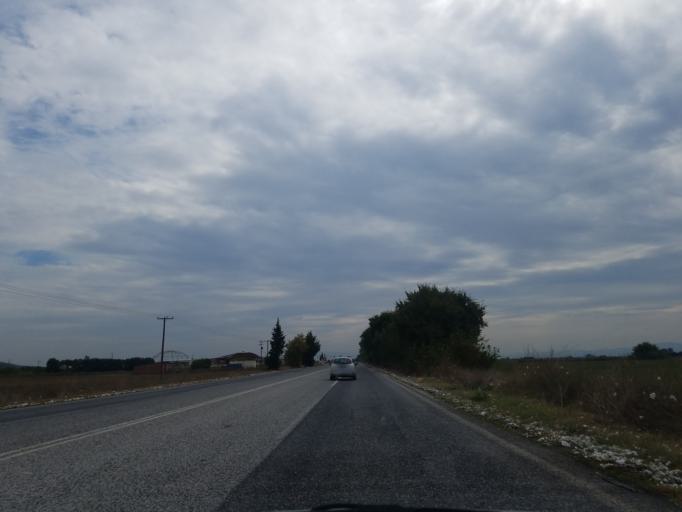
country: GR
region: Thessaly
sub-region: Nomos Kardhitsas
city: Karpochori
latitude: 39.3641
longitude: 22.0332
